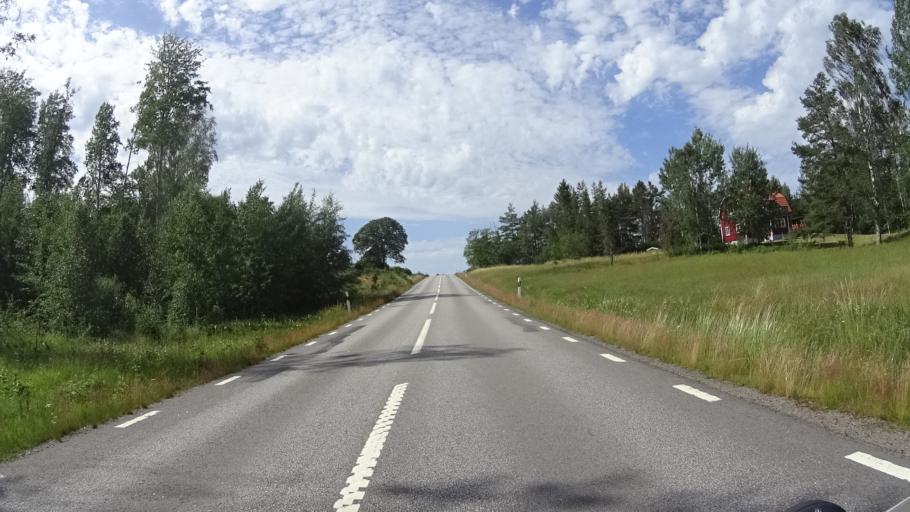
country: SE
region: OEstergoetland
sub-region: Atvidabergs Kommun
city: Atvidaberg
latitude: 58.0840
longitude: 16.1470
